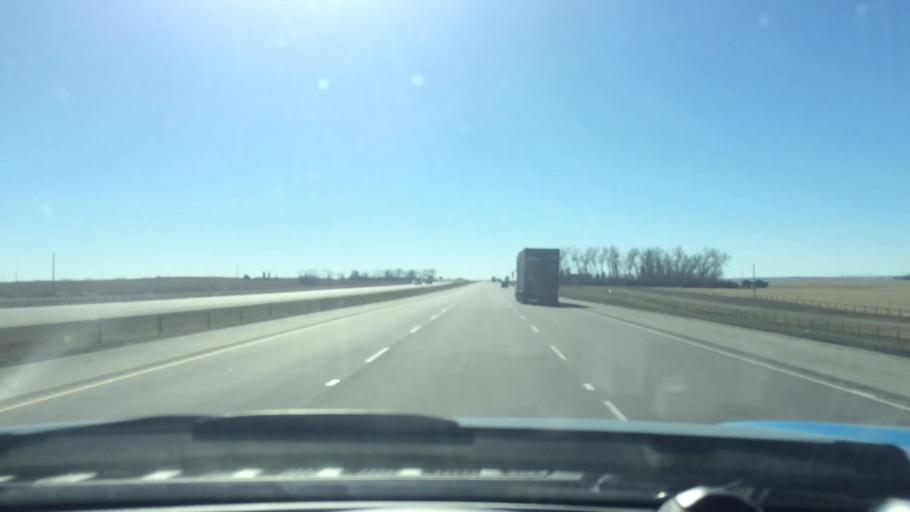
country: CA
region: Alberta
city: Crossfield
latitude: 51.4080
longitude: -114.0021
